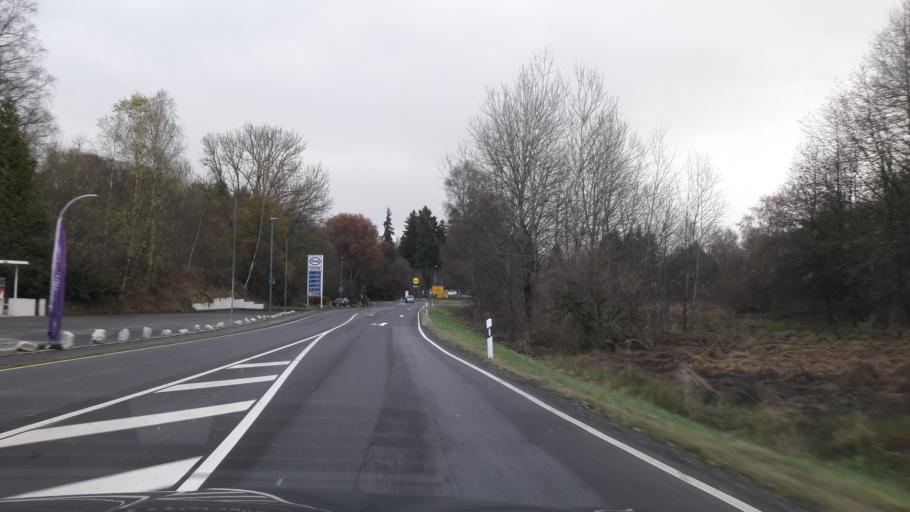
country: DE
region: Rheinland-Pfalz
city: Hermeskeil
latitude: 49.6605
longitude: 6.9279
